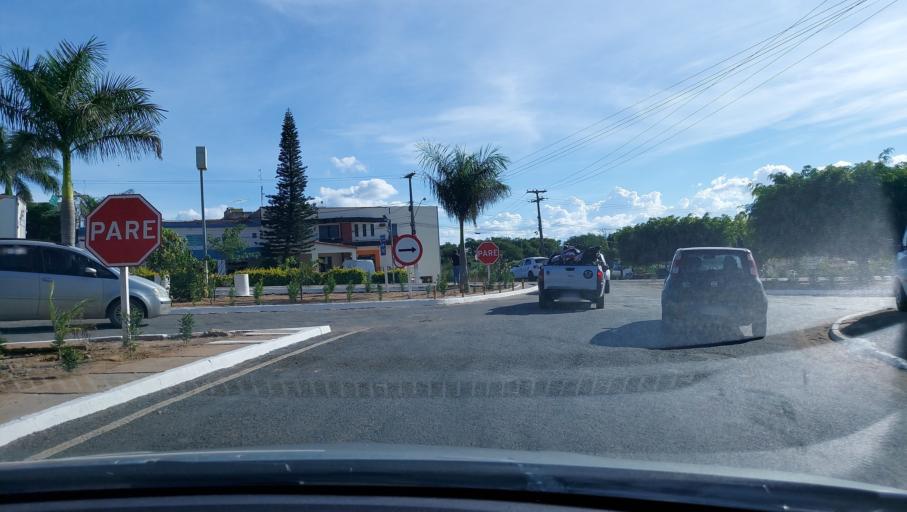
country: BR
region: Bahia
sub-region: Seabra
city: Seabra
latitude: -12.4270
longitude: -41.7694
